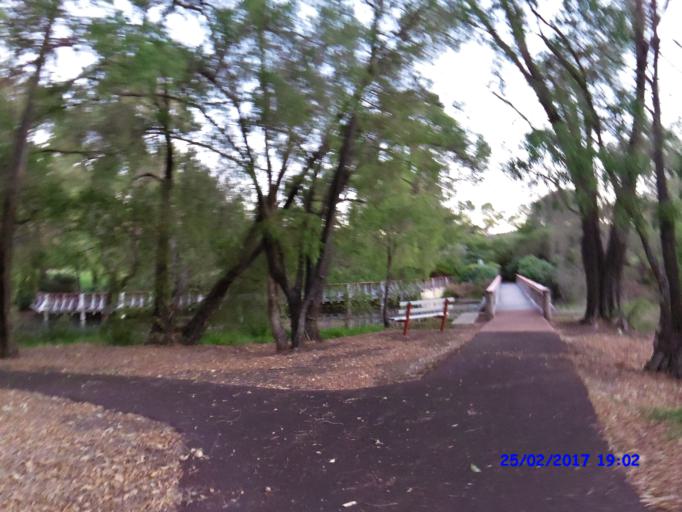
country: AU
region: Western Australia
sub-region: Harvey
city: Harvey
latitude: -33.0791
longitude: 115.9277
